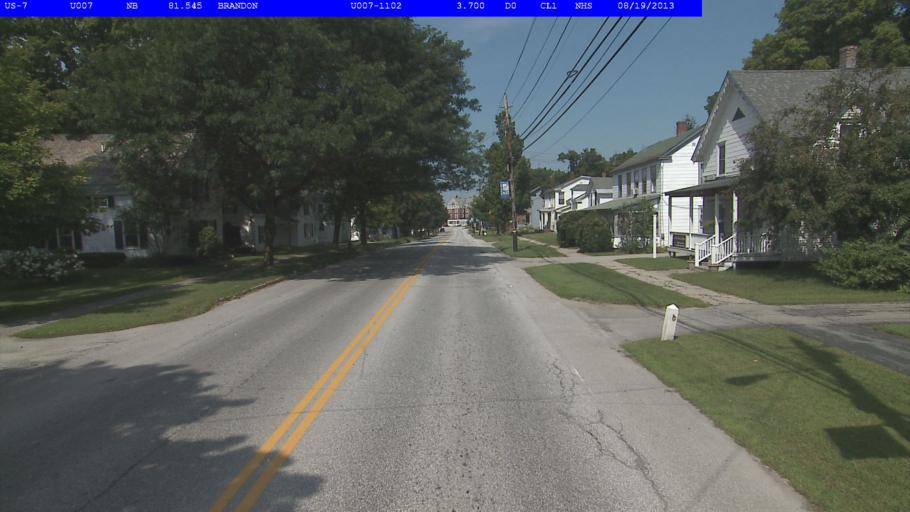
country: US
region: Vermont
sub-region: Rutland County
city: Brandon
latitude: 43.7969
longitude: -73.0834
